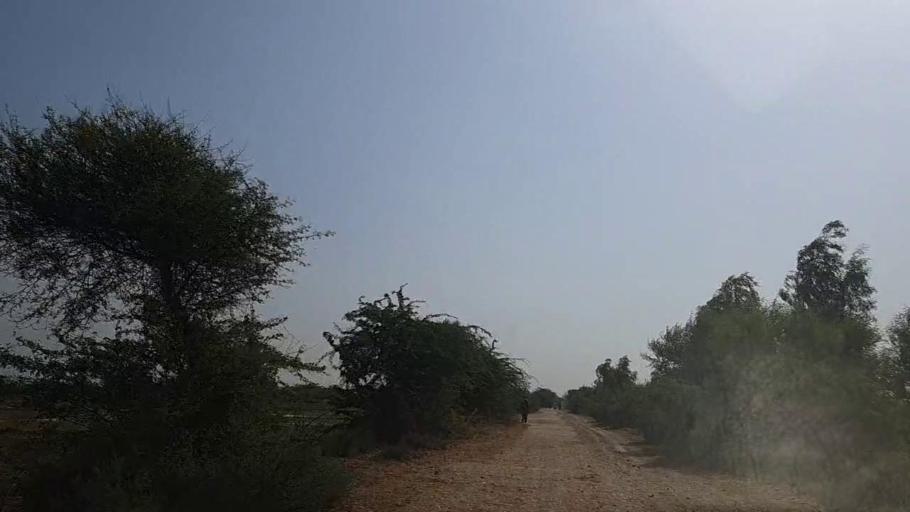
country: PK
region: Sindh
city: Daro Mehar
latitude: 24.7208
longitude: 68.0766
